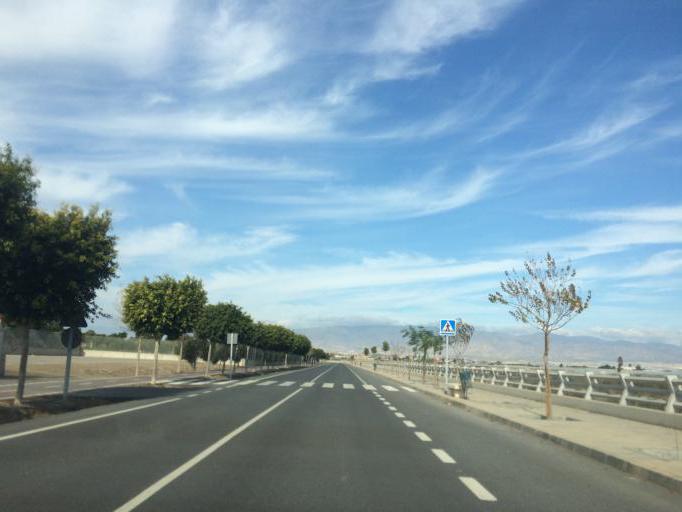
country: ES
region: Andalusia
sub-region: Provincia de Almeria
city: Almeria
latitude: 36.8232
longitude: -2.4286
